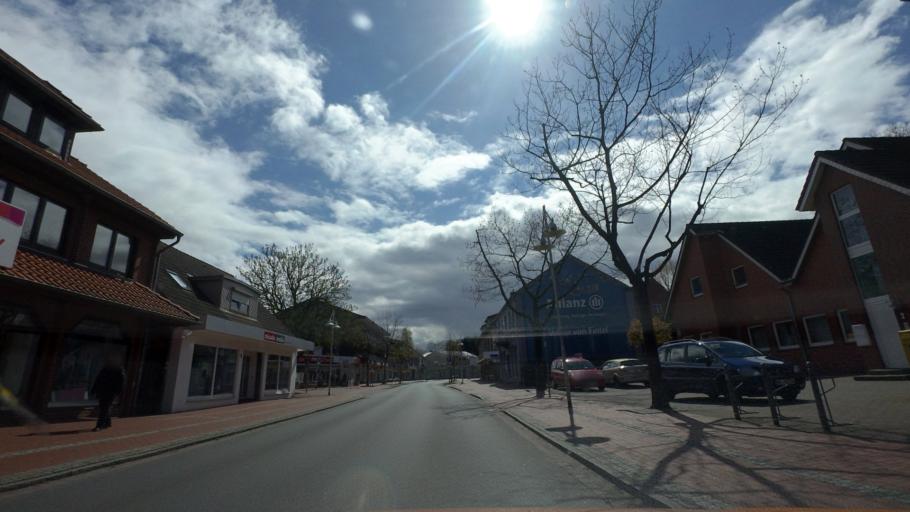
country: DE
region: Lower Saxony
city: Schneverdingen
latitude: 53.1180
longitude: 9.7880
